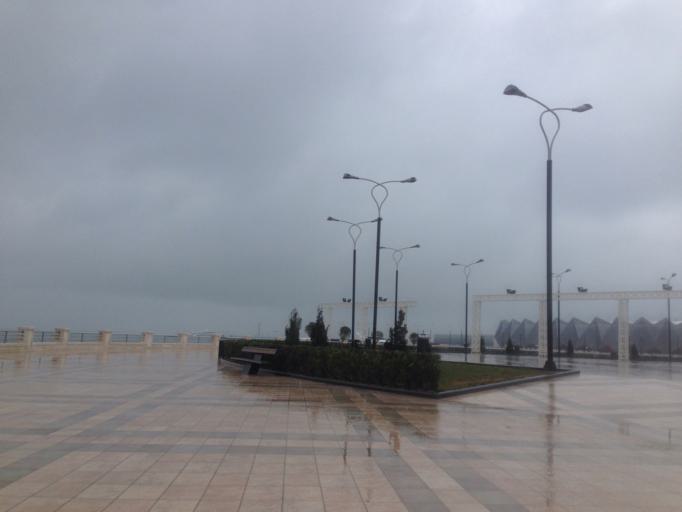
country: AZ
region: Baki
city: Badamdar
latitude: 40.3480
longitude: 49.8457
